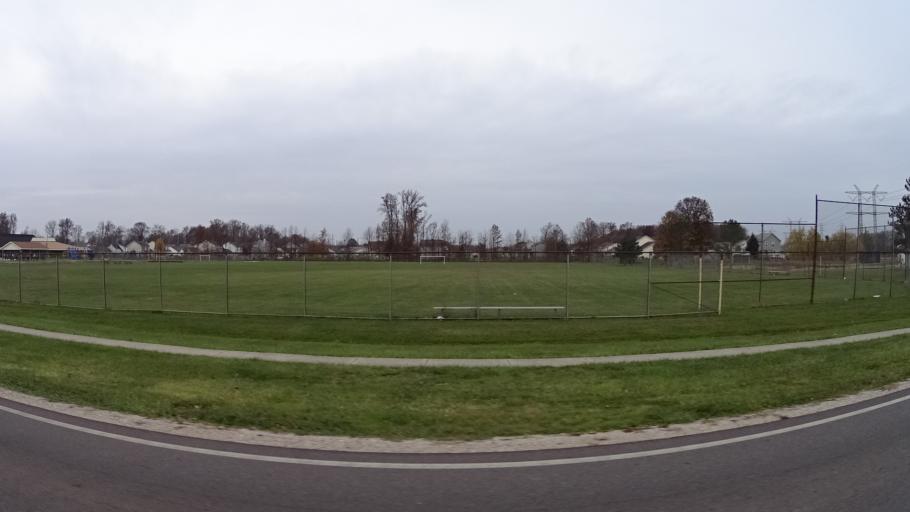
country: US
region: Ohio
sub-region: Lorain County
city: North Ridgeville
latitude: 41.4077
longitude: -82.0064
